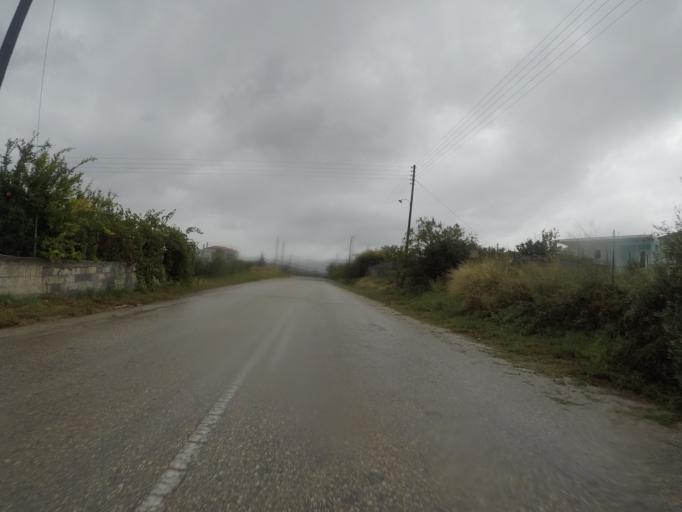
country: GR
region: Peloponnese
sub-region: Nomos Korinthias
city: Arkhaia Korinthos
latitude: 37.9021
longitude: 22.8867
